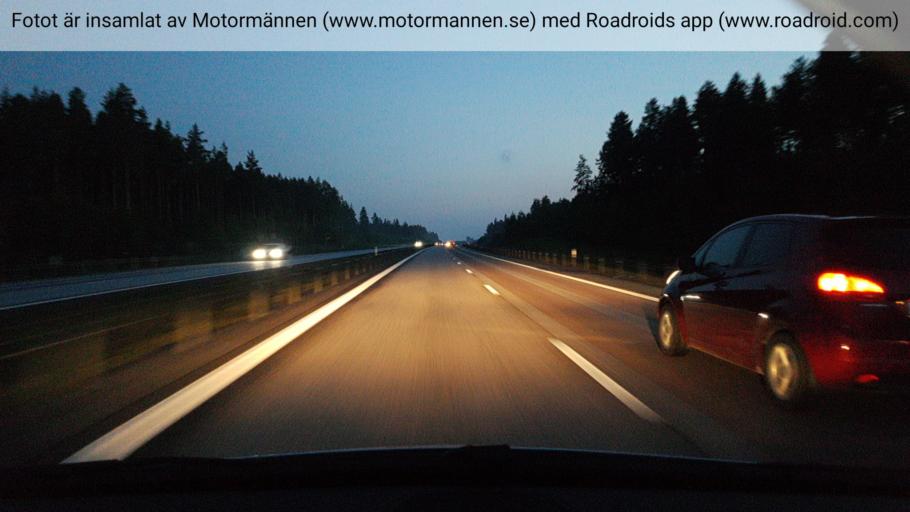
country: SE
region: Uppsala
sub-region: Tierps Kommun
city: Tierp
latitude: 60.2303
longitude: 17.5006
